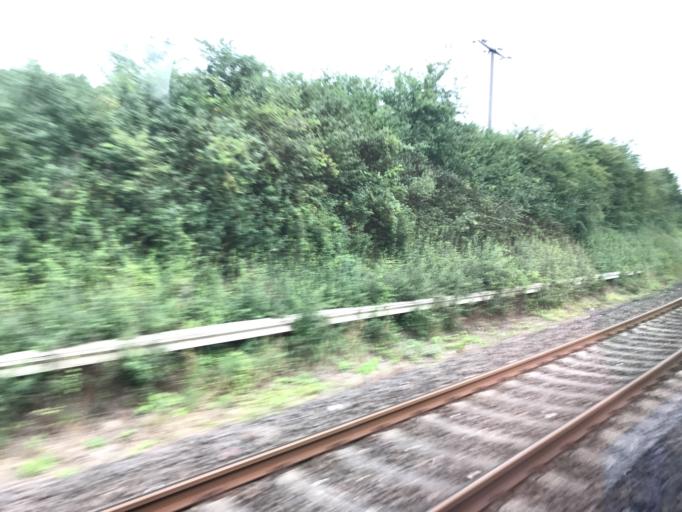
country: DE
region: Hesse
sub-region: Regierungsbezirk Giessen
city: Villmar
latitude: 50.3920
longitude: 8.1814
